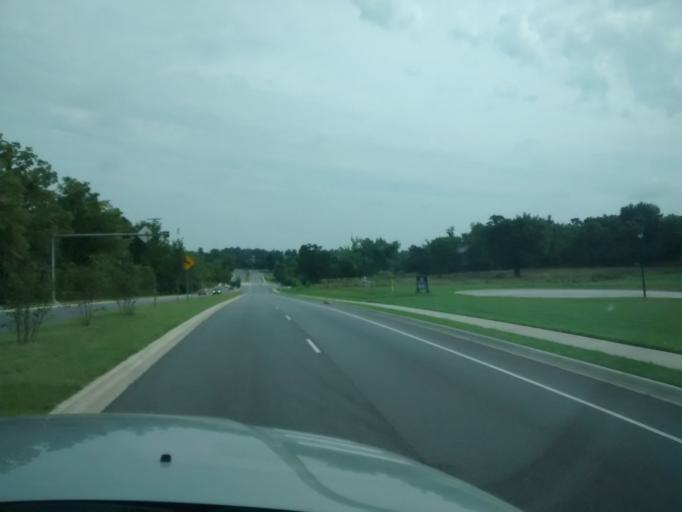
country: US
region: Arkansas
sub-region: Washington County
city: Johnson
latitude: 36.1386
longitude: -94.1177
